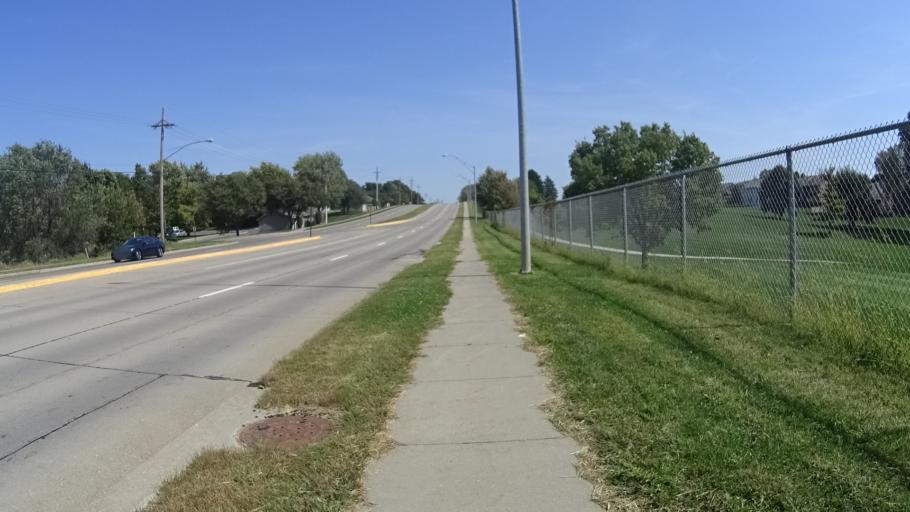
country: US
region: Nebraska
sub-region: Sarpy County
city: La Vista
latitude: 41.1761
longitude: -96.0525
